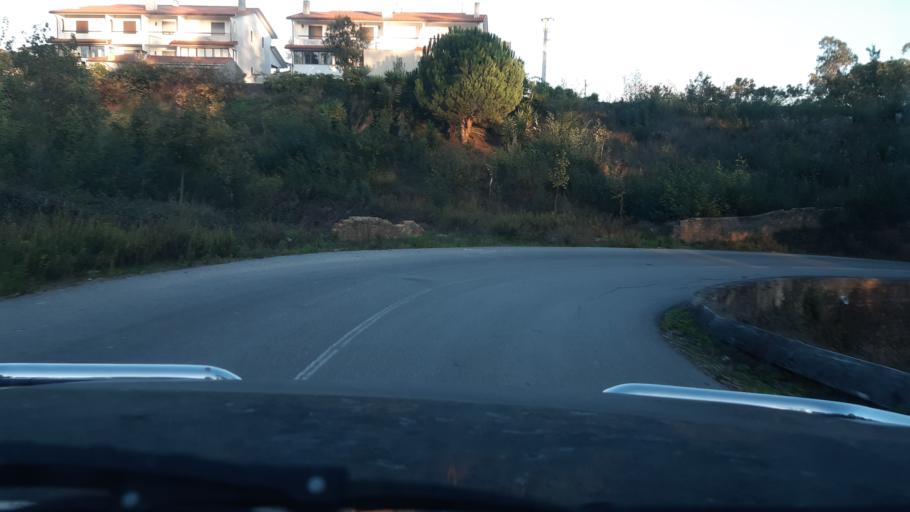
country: PT
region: Aveiro
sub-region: Agueda
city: Agueda
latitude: 40.5783
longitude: -8.4631
